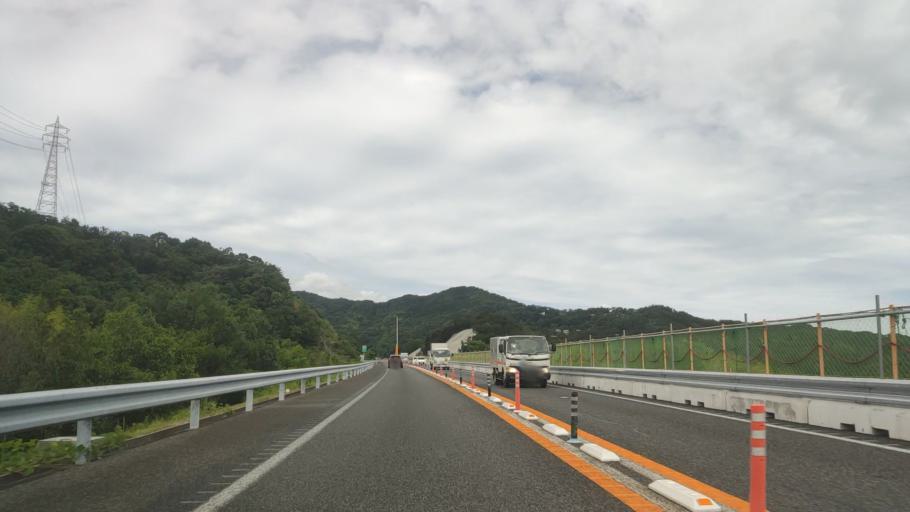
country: JP
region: Wakayama
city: Gobo
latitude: 33.8399
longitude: 135.2203
